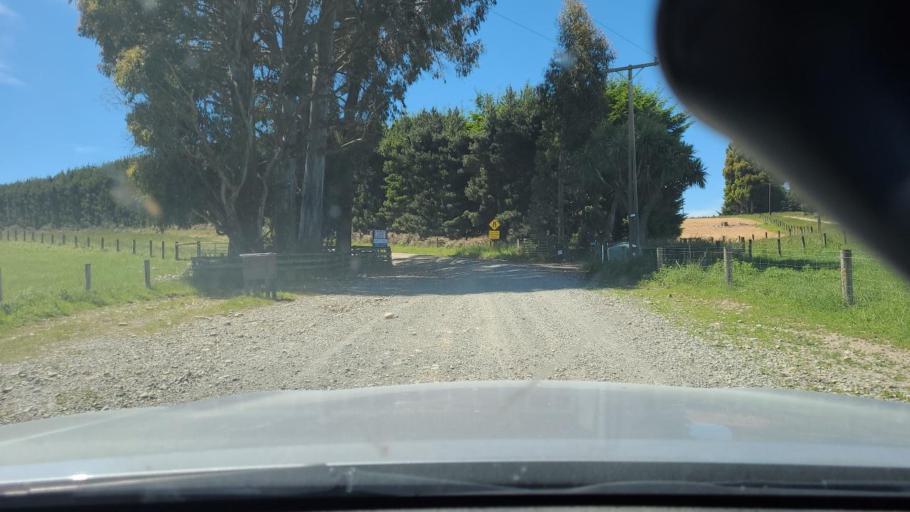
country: NZ
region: Southland
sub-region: Southland District
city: Te Anau
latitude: -45.4805
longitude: 167.9278
